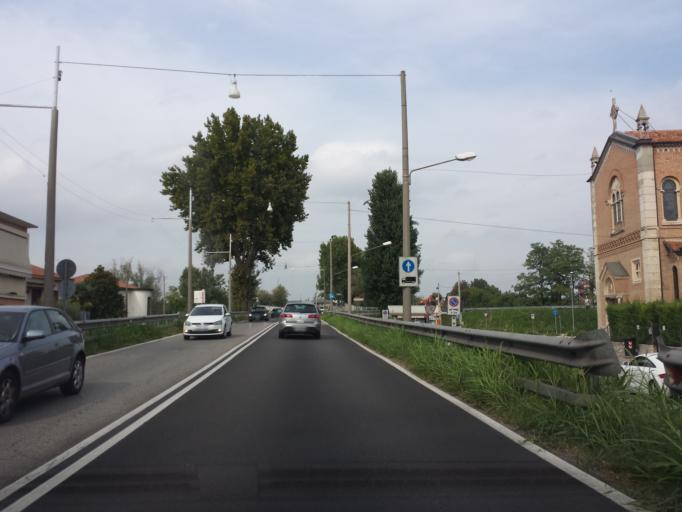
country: IT
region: Veneto
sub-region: Provincia di Padova
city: Vigodarzere
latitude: 45.4452
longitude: 11.8936
